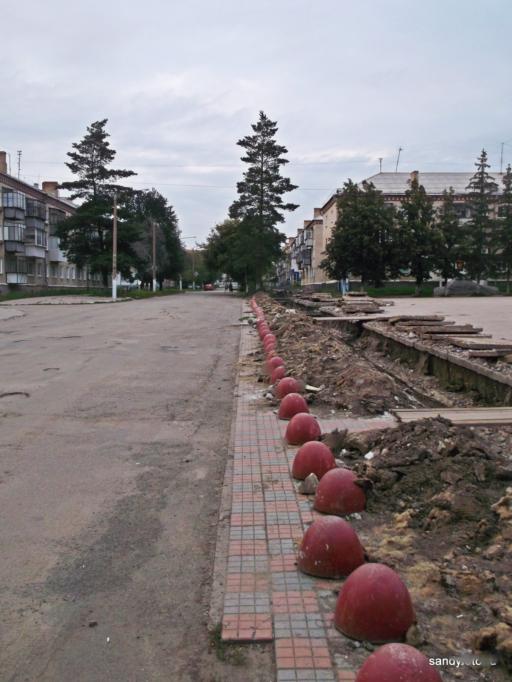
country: RU
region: Chelyabinsk
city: Troitsk
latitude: 54.0461
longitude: 61.6290
